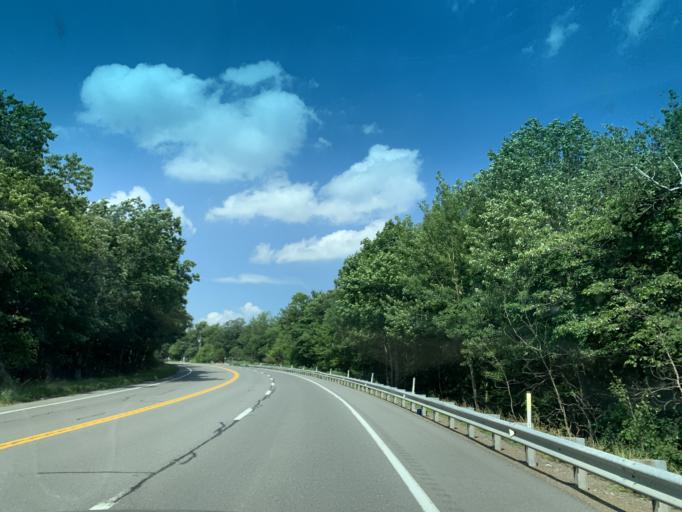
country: US
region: Pennsylvania
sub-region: Schuylkill County
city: Ashland
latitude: 40.8103
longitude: -76.3338
